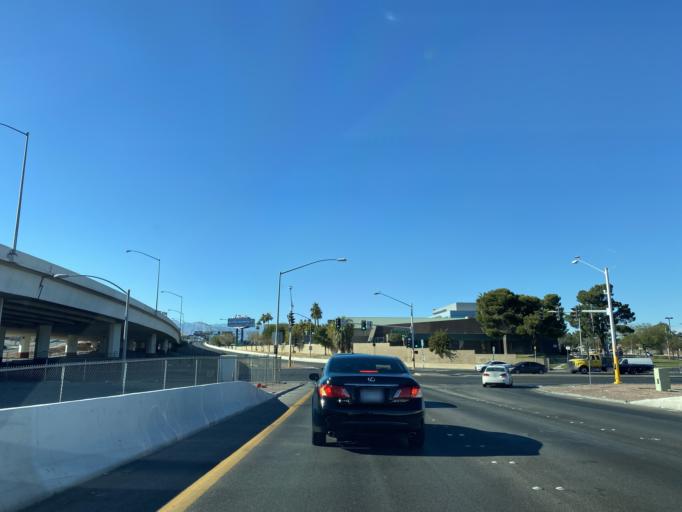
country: US
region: Nevada
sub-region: Clark County
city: Las Vegas
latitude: 36.1737
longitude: -115.1371
